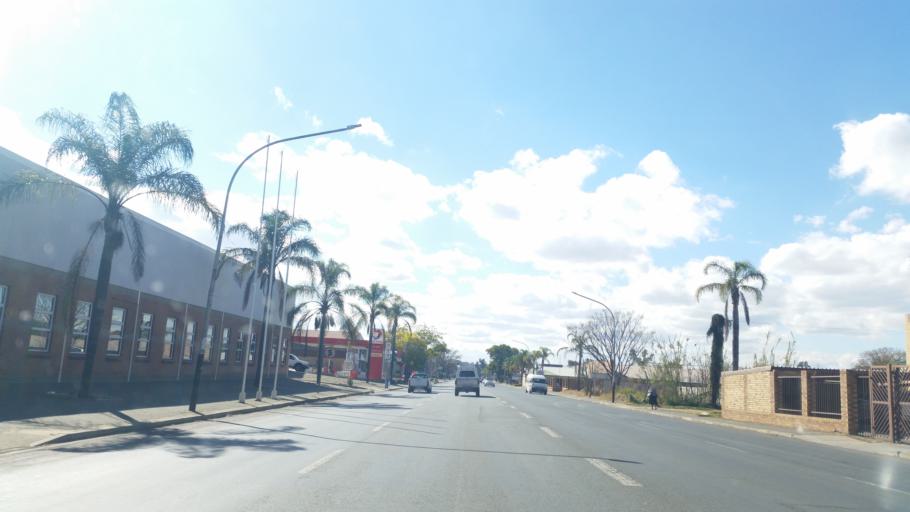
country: ZA
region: KwaZulu-Natal
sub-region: uThukela District Municipality
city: Ladysmith
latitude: -28.5674
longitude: 29.7778
